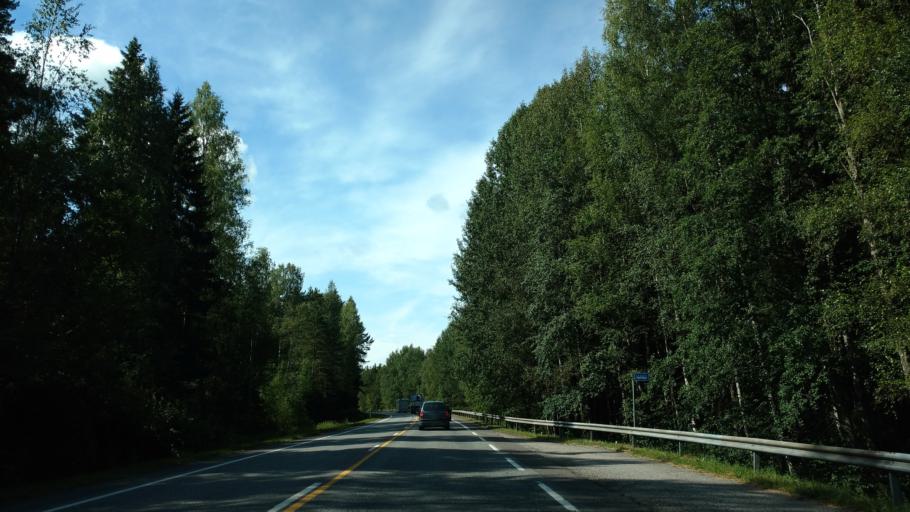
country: FI
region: Varsinais-Suomi
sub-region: Salo
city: Salo
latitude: 60.3434
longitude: 23.1313
